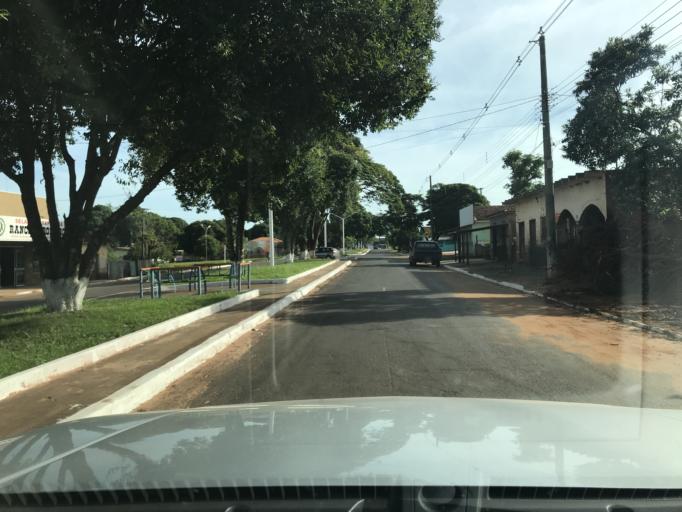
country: BR
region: Mato Grosso do Sul
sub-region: Iguatemi
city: Iguatemi
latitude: -23.6654
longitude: -54.5622
